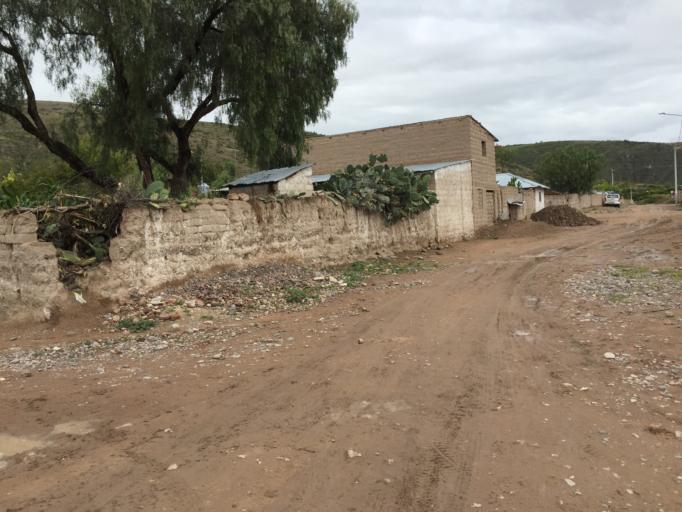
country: PE
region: Ayacucho
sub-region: Provincia de Huamanga
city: Ayacucho
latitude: -13.1294
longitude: -74.2319
